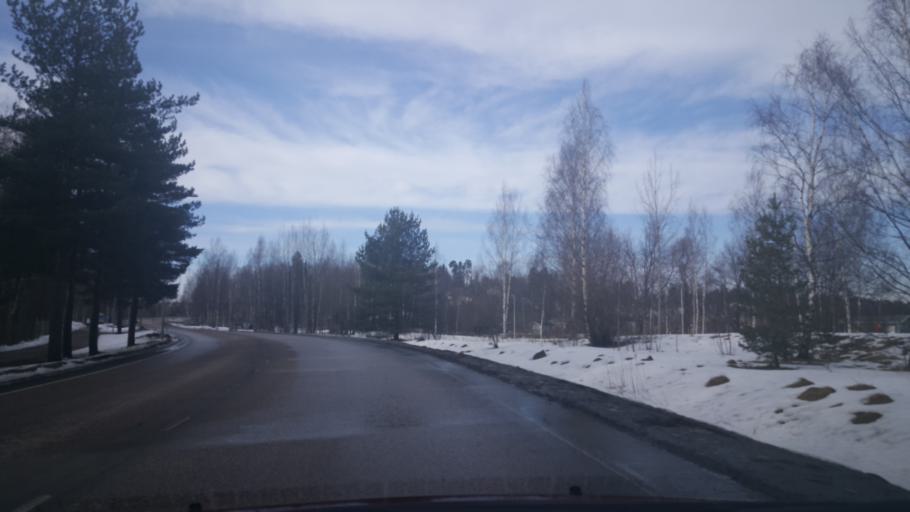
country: FI
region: Uusimaa
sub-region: Helsinki
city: Teekkarikylae
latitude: 60.2726
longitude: 24.8777
